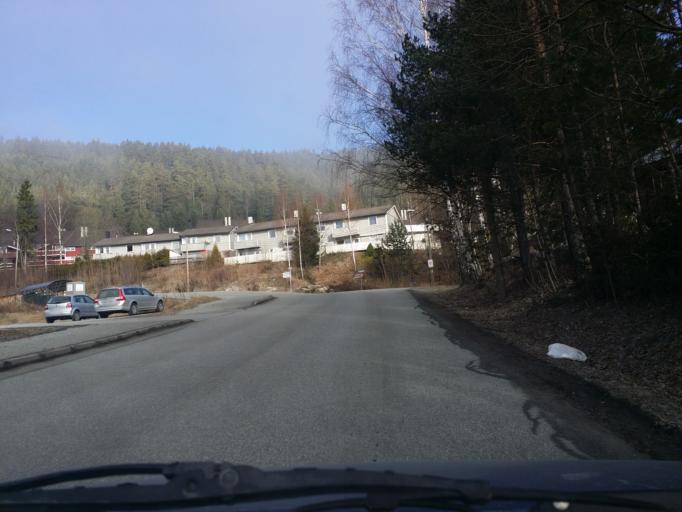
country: NO
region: Buskerud
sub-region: Nedre Eiker
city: Mjondalen
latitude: 59.7623
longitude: 10.0318
